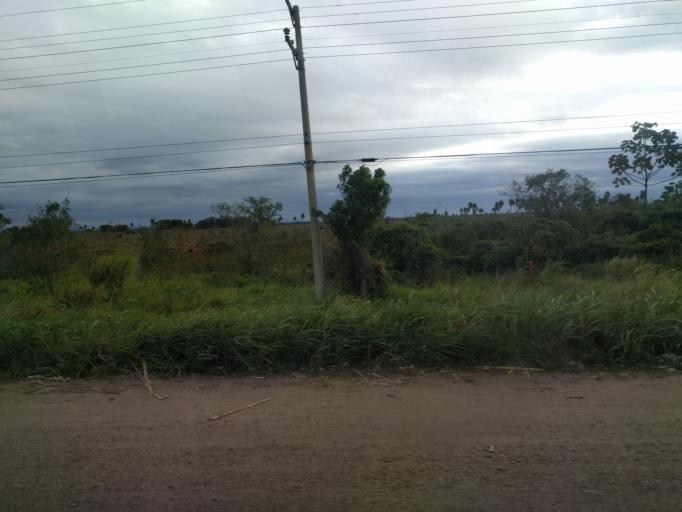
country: BO
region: Santa Cruz
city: La Belgica
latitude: -17.6208
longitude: -63.1590
